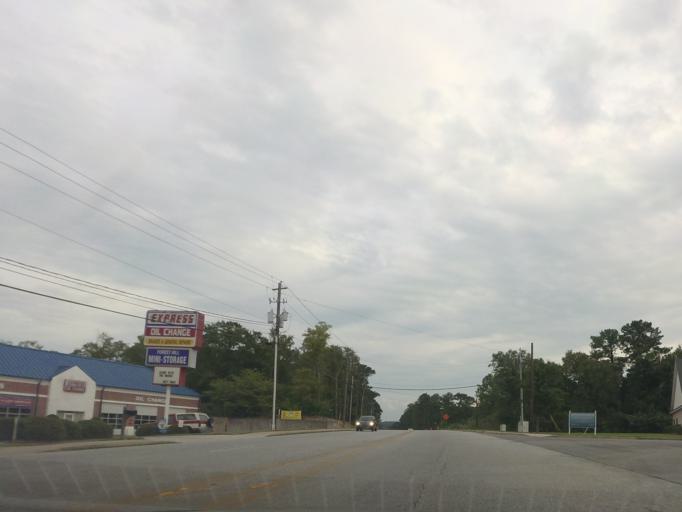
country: US
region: Georgia
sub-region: Bibb County
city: Macon
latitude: 32.8973
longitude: -83.7025
